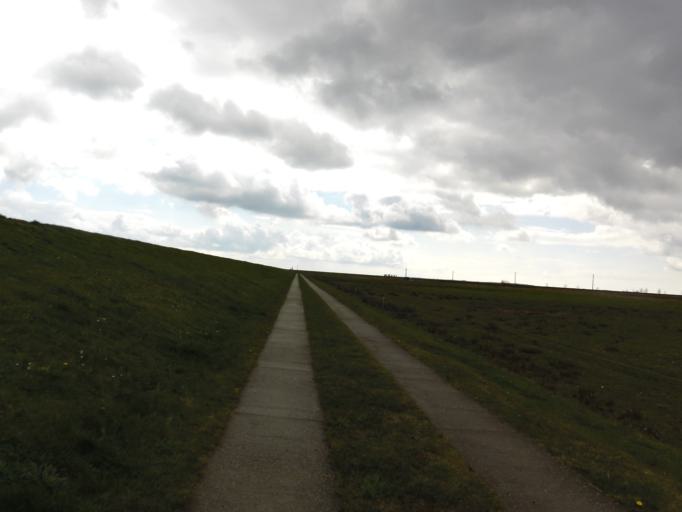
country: DE
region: Mecklenburg-Vorpommern
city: Barth
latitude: 54.4185
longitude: 12.7971
